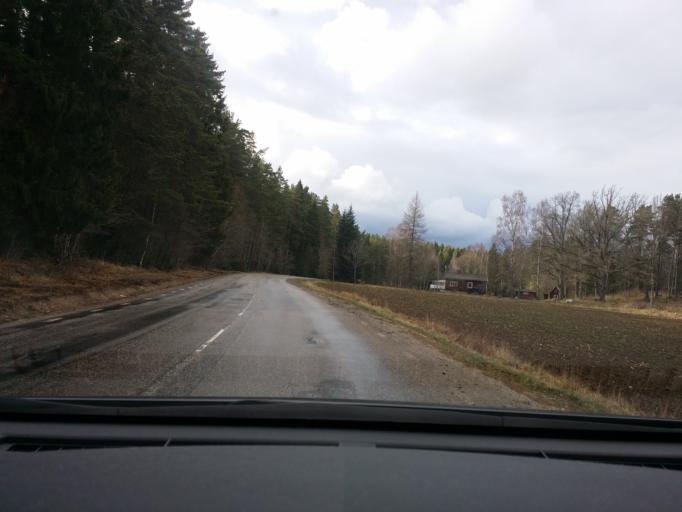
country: SE
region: Soedermanland
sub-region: Eskilstuna Kommun
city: Arla
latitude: 59.3102
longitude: 16.6820
